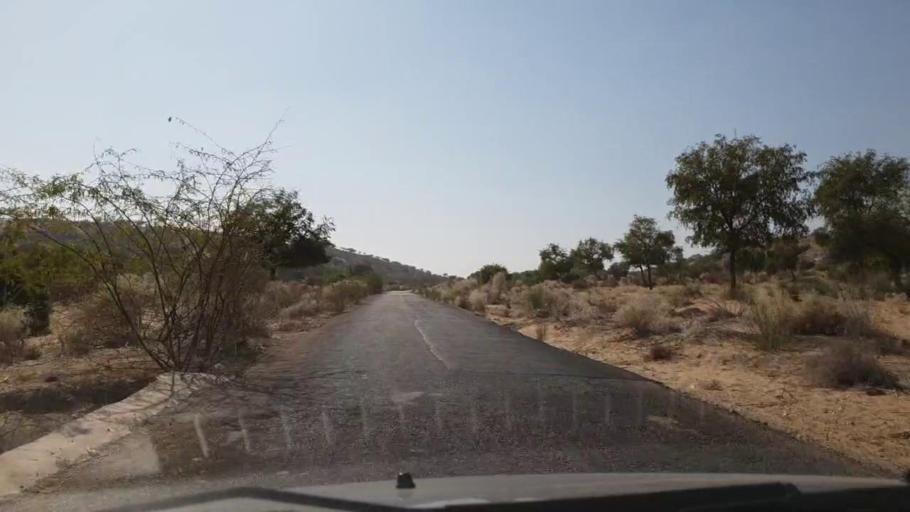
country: PK
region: Sindh
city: Mithi
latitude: 24.6792
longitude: 69.7770
